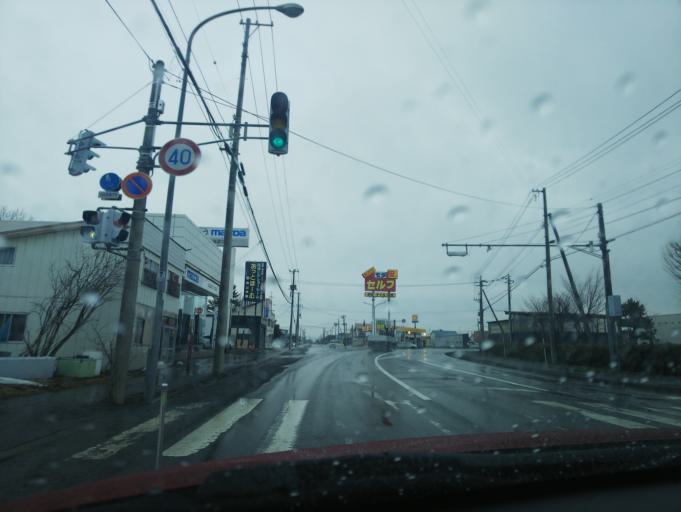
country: JP
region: Hokkaido
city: Nayoro
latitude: 44.1857
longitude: 142.3893
